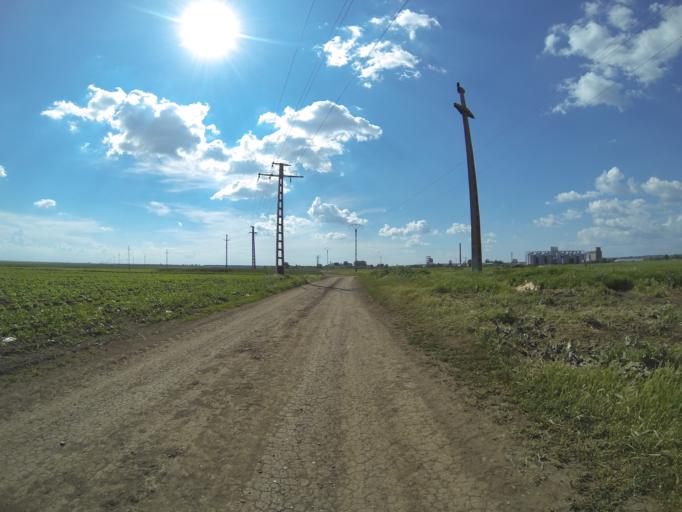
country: RO
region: Dolj
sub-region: Comuna Segarcea
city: Segarcea
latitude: 44.0787
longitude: 23.7345
